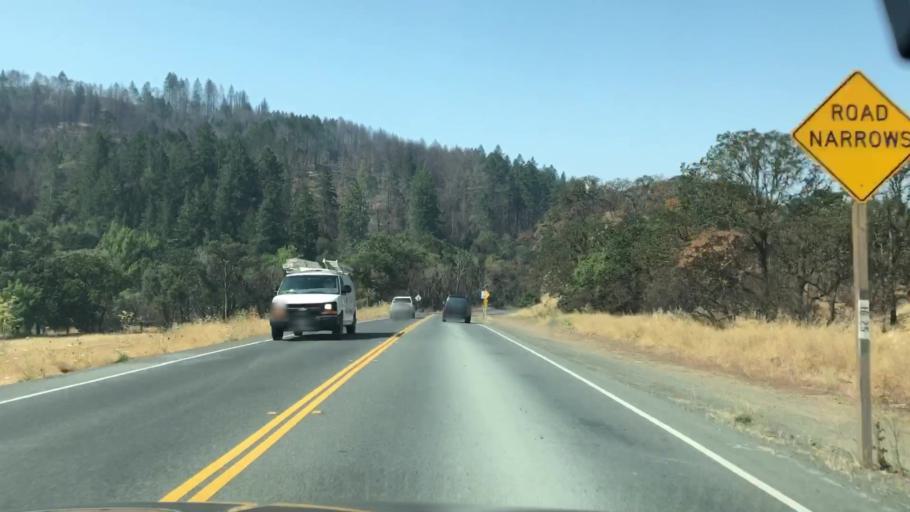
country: US
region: California
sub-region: Sonoma County
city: Larkfield-Wikiup
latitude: 38.5498
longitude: -122.7069
